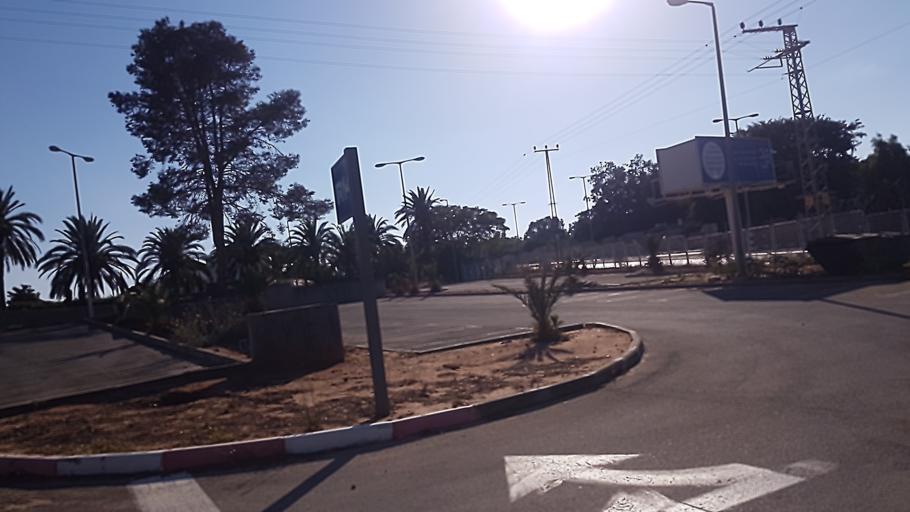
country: IL
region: Central District
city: Kfar Saba
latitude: 32.2015
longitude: 34.9184
